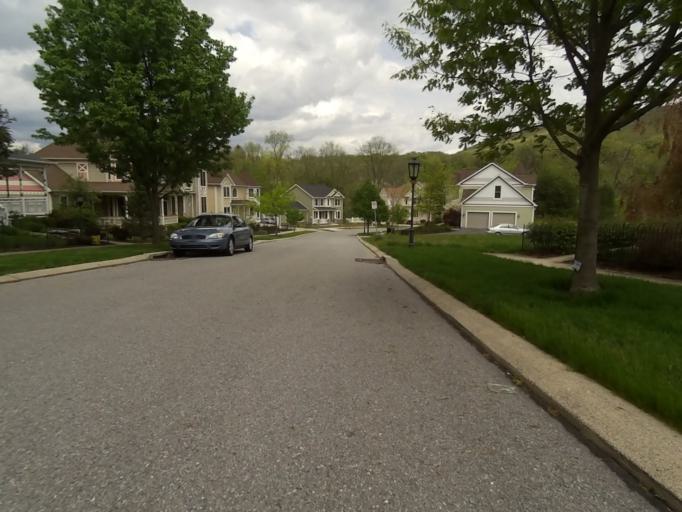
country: US
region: Pennsylvania
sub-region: Centre County
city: Lemont
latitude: 40.8115
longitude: -77.8210
